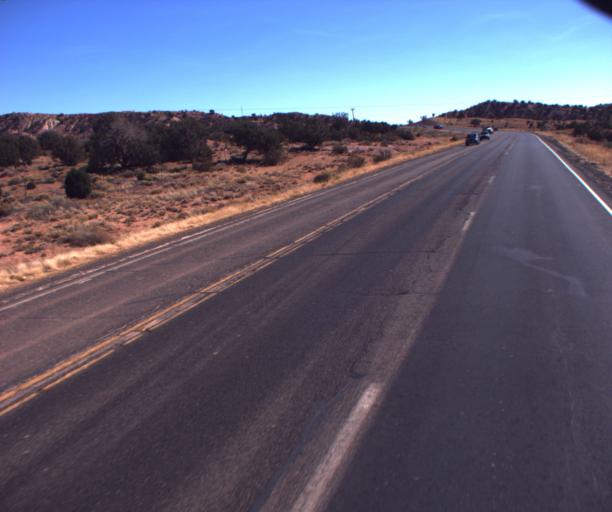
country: US
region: Arizona
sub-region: Apache County
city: Ganado
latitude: 35.7480
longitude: -109.6216
